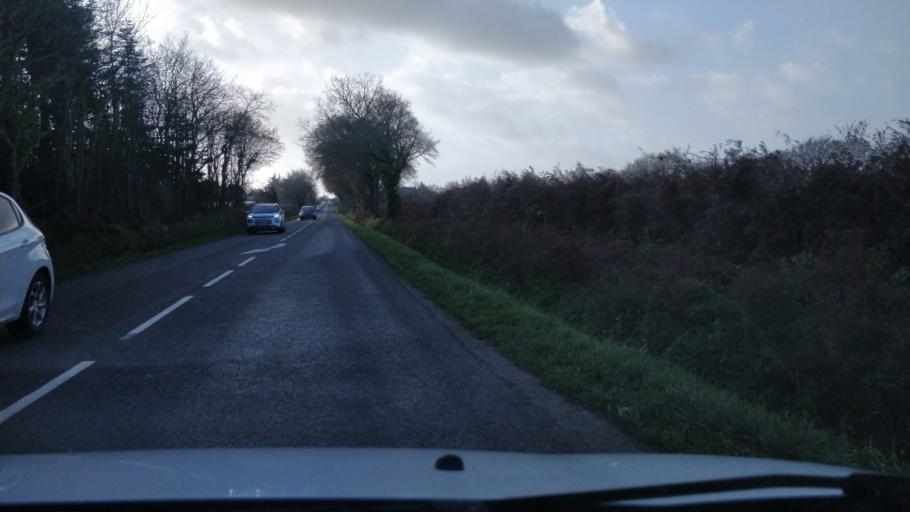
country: FR
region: Pays de la Loire
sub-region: Departement de la Loire-Atlantique
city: Saint-Molf
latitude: 47.3609
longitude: -2.4314
